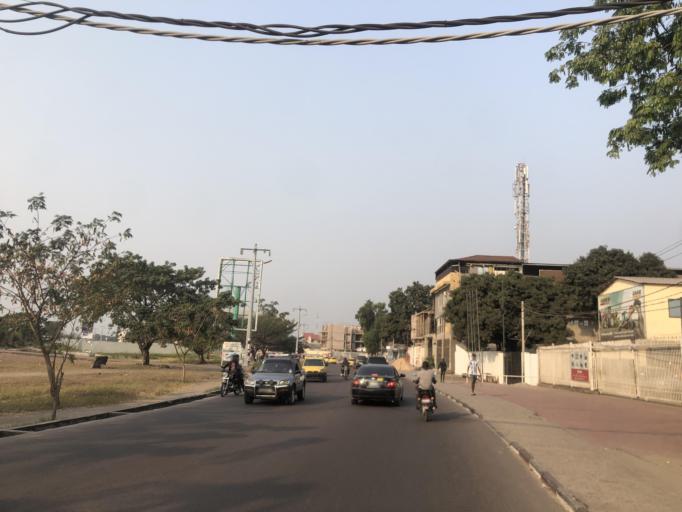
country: CD
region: Kinshasa
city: Kinshasa
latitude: -4.3301
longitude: 15.3282
